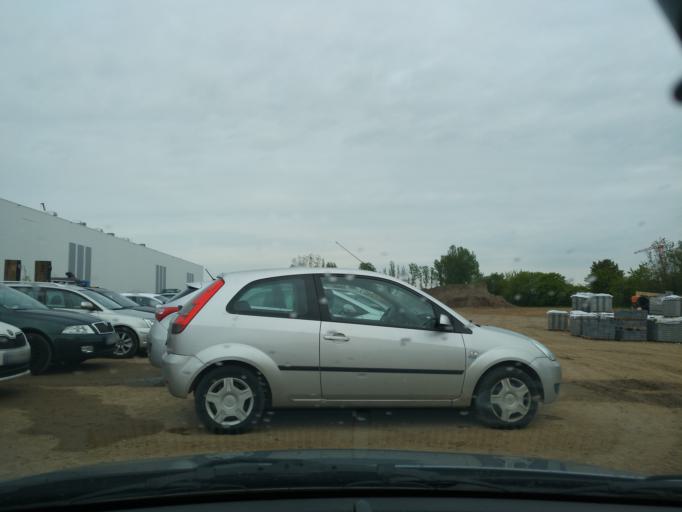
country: DE
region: Berlin
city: Mahlsdorf
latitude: 52.5002
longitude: 13.6212
